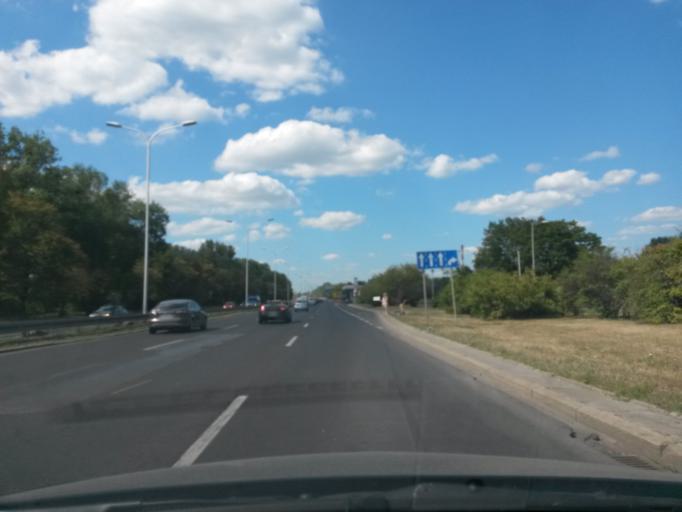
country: PL
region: Masovian Voivodeship
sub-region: Warszawa
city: Zoliborz
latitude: 52.2753
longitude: 20.9951
